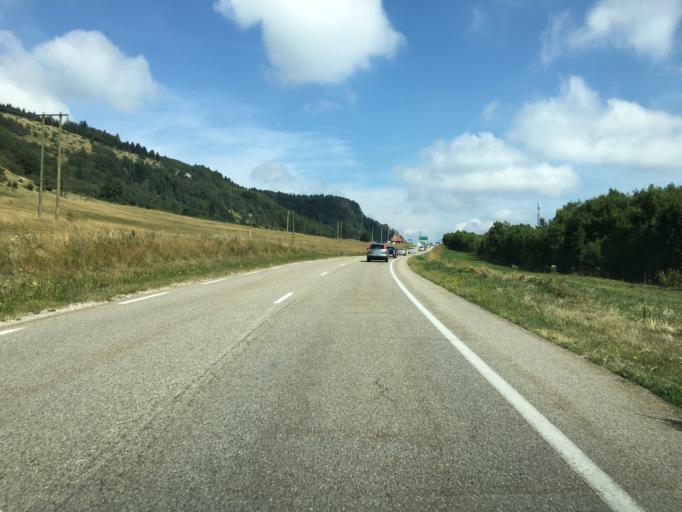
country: FR
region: Rhone-Alpes
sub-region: Departement de l'Isere
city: Mens
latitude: 44.7205
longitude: 5.6766
